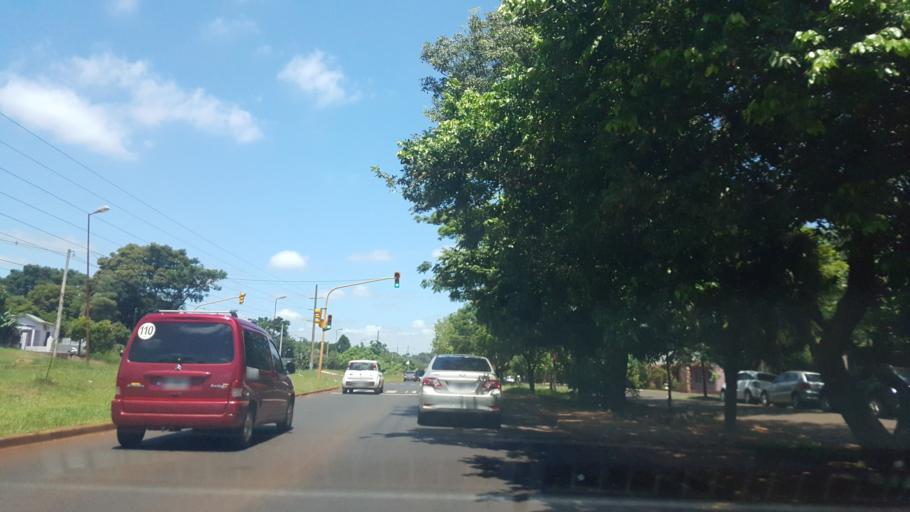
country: AR
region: Misiones
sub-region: Departamento de Capital
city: Posadas
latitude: -27.4148
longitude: -55.9285
